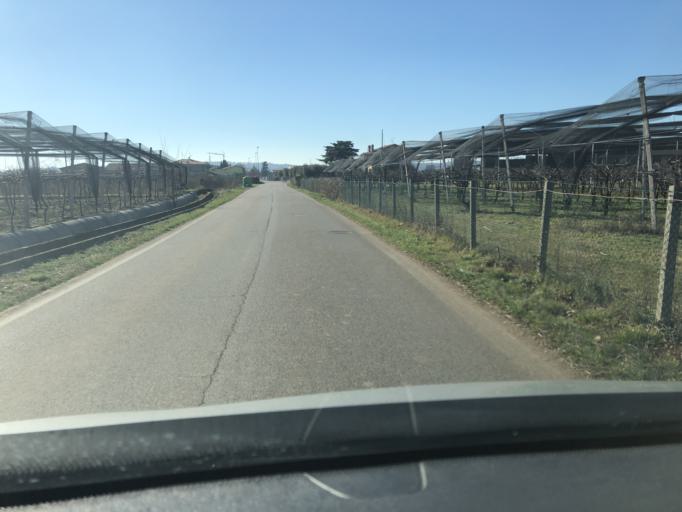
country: IT
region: Veneto
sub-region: Provincia di Verona
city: Bussolengo
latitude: 45.4590
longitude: 10.8694
